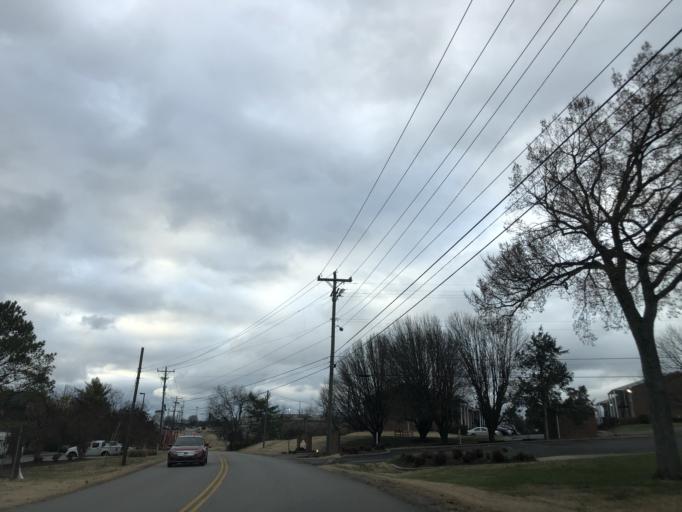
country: US
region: Tennessee
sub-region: Davidson County
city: Goodlettsville
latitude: 36.3000
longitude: -86.6897
